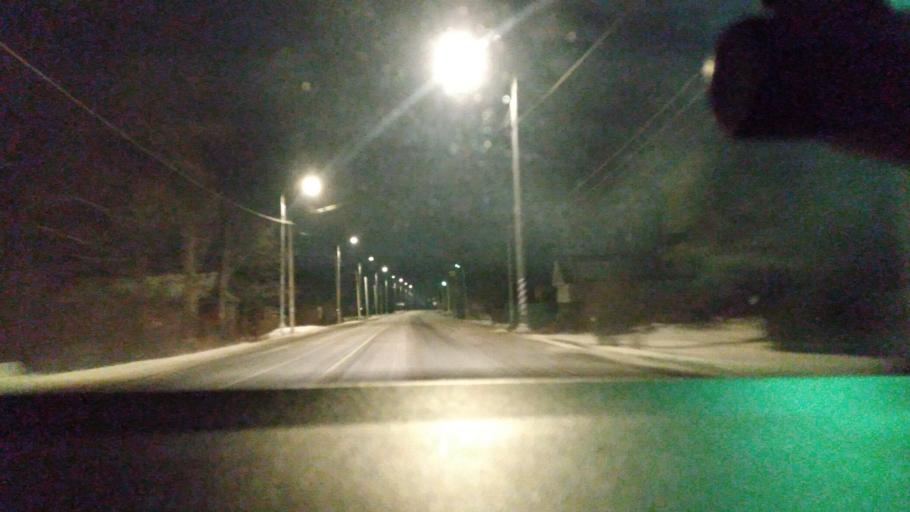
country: RU
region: Moskovskaya
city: Lukhovitsy
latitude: 55.0997
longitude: 38.9824
